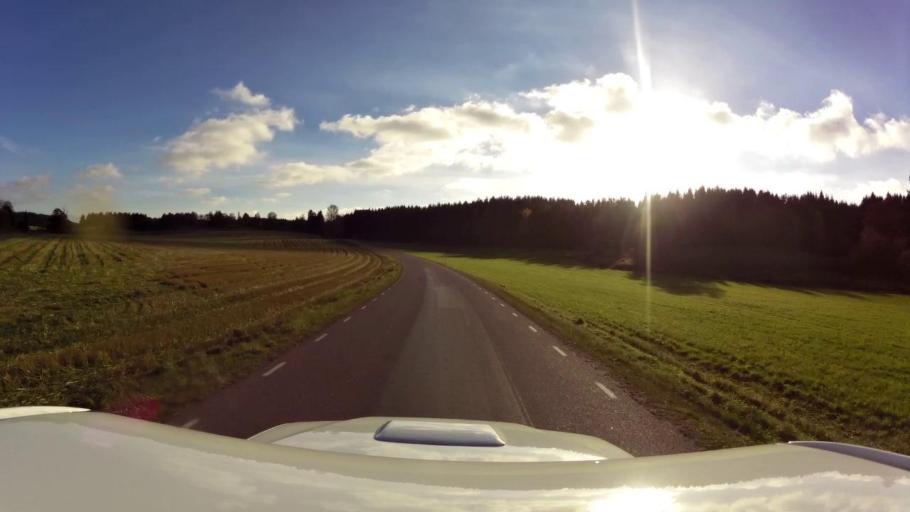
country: SE
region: OEstergoetland
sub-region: Linkopings Kommun
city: Vikingstad
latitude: 58.2781
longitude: 15.4345
